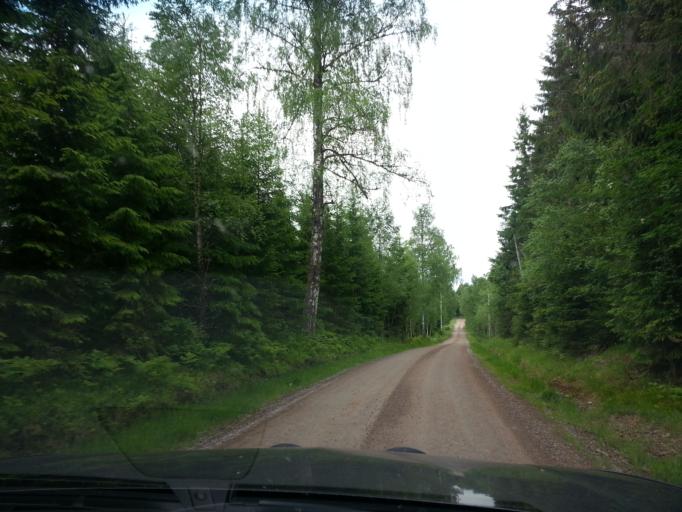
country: SE
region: Joenkoeping
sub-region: Vetlanda Kommun
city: Vetlanda
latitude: 57.2841
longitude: 15.1394
